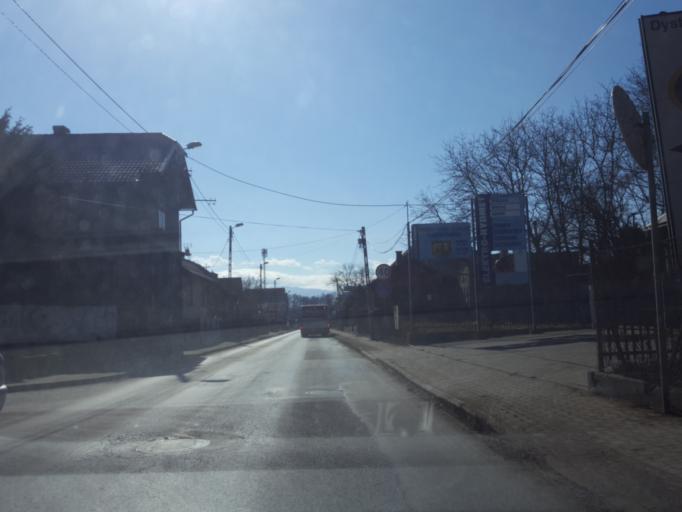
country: PL
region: Lesser Poland Voivodeship
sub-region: Powiat nowosadecki
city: Nowy Sacz
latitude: 49.6000
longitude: 20.6909
